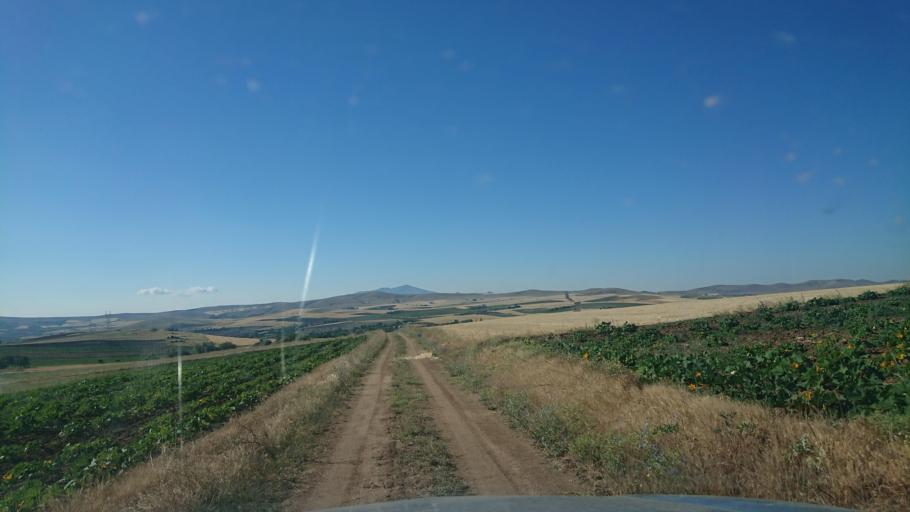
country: TR
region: Aksaray
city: Agacoren
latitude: 38.8361
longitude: 33.9381
